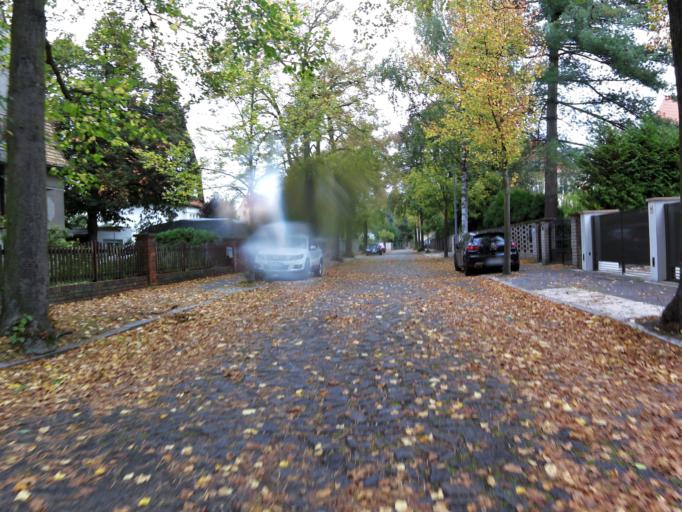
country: DE
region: Saxony
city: Markkleeberg
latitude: 51.2910
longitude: 12.3715
